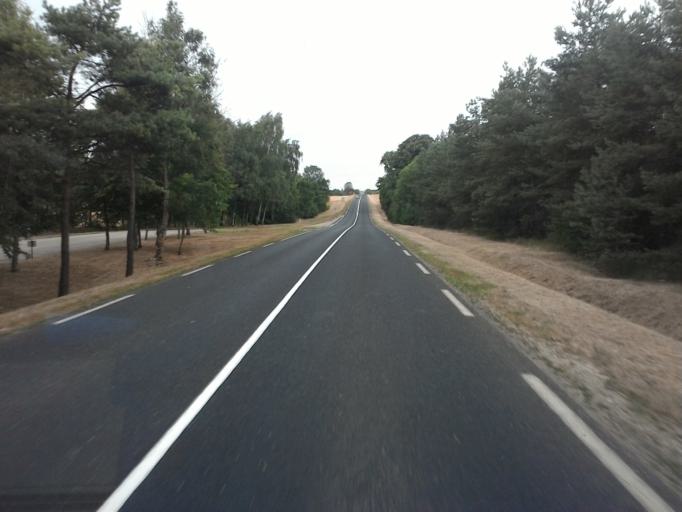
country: FR
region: Lorraine
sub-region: Departement de Meurthe-et-Moselle
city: Colombey-les-Belles
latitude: 48.5135
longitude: 5.8856
